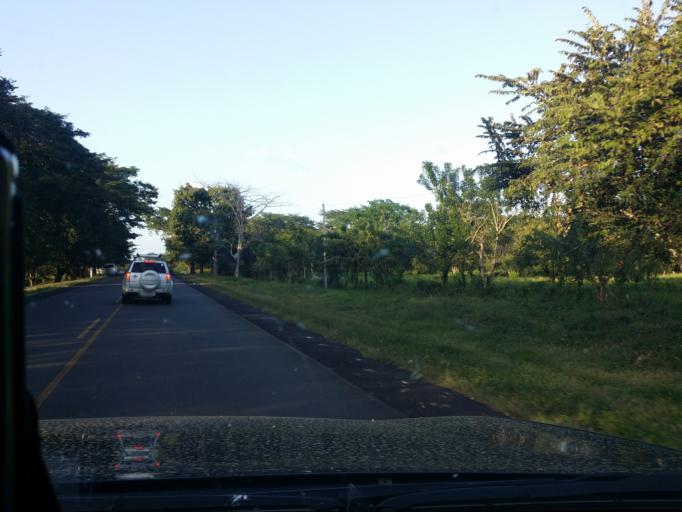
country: NI
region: Rio San Juan
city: San Miguelito
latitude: 11.5017
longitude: -84.8368
